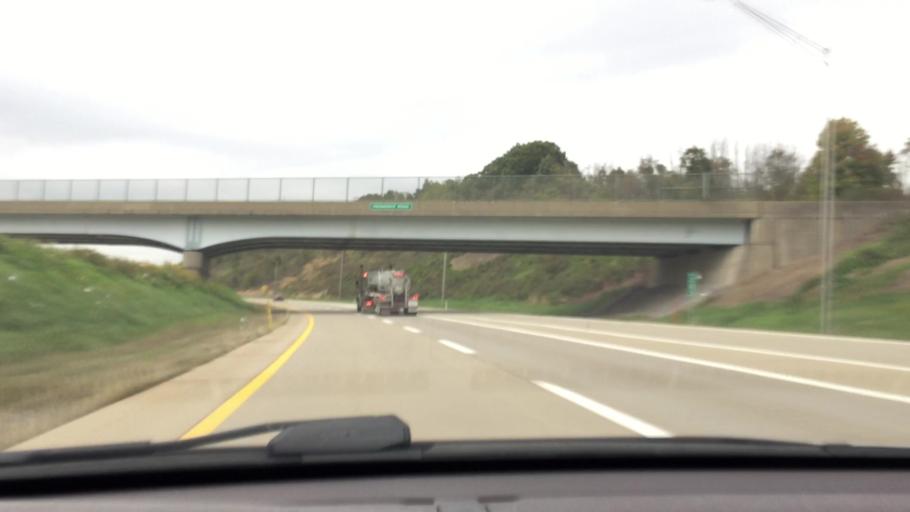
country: US
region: Pennsylvania
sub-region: Beaver County
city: Big Beaver
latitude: 40.8013
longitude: -80.3614
